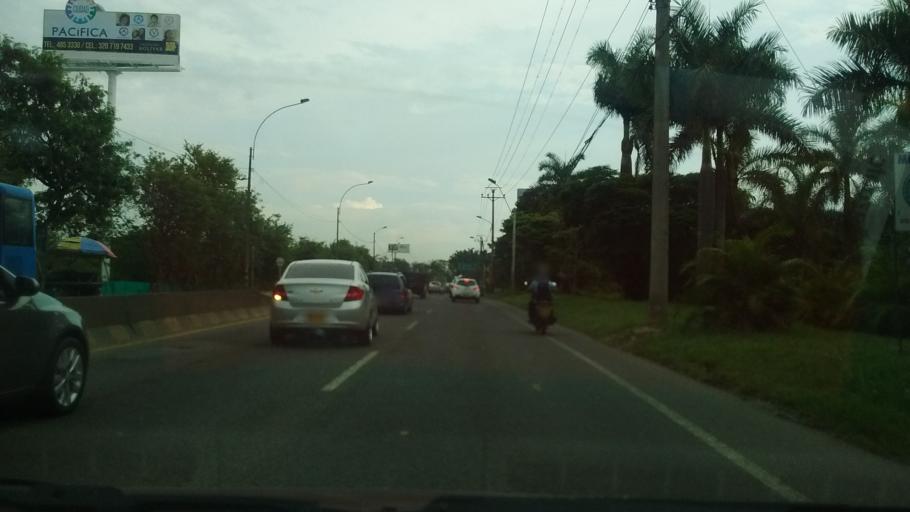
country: CO
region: Valle del Cauca
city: Jamundi
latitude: 3.3470
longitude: -76.5242
